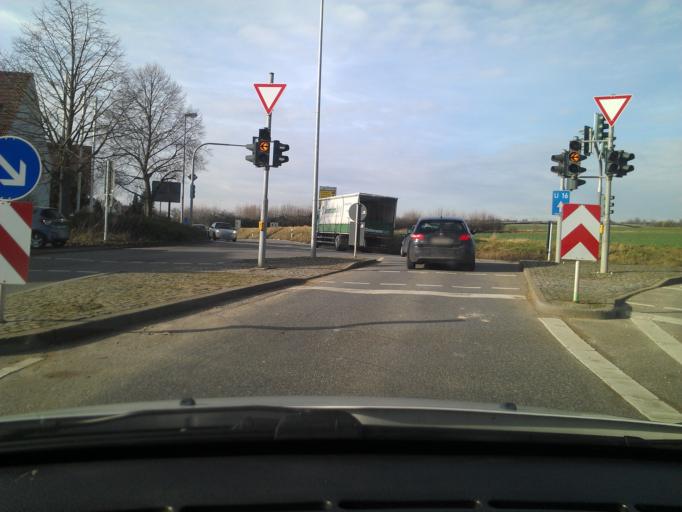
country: DE
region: Baden-Wuerttemberg
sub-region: Regierungsbezirk Stuttgart
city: Neuhausen auf den Fildern
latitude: 48.6901
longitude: 9.2814
